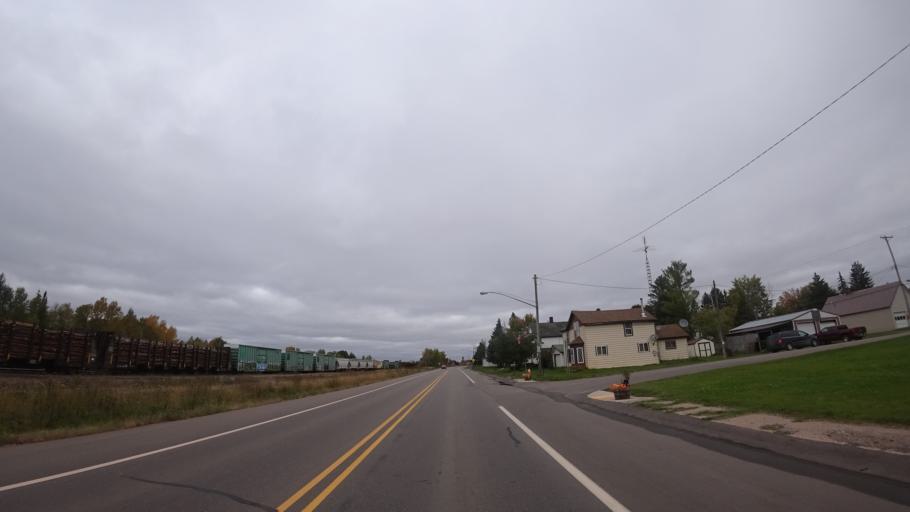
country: US
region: Michigan
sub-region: Iron County
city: Crystal Falls
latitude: 46.1414
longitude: -88.0939
